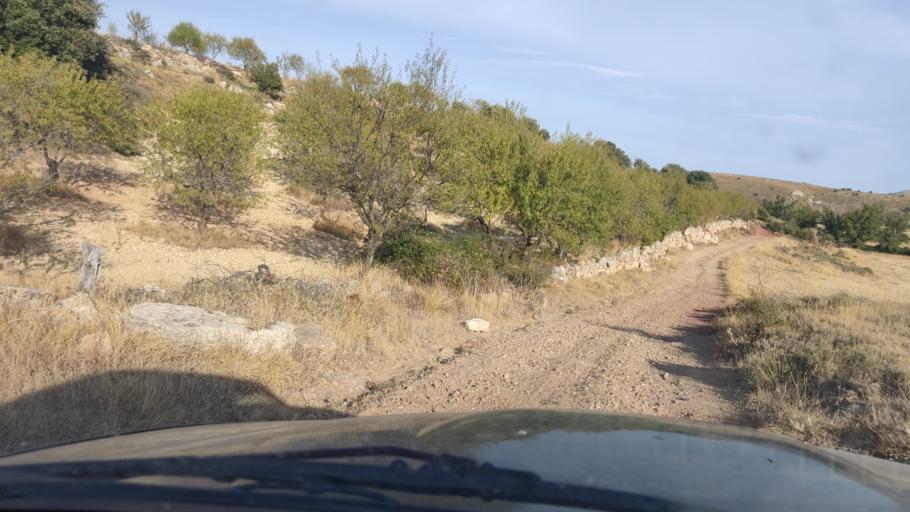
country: ES
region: Aragon
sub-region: Provincia de Teruel
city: Monforte de Moyuela
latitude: 41.0313
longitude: -1.0128
